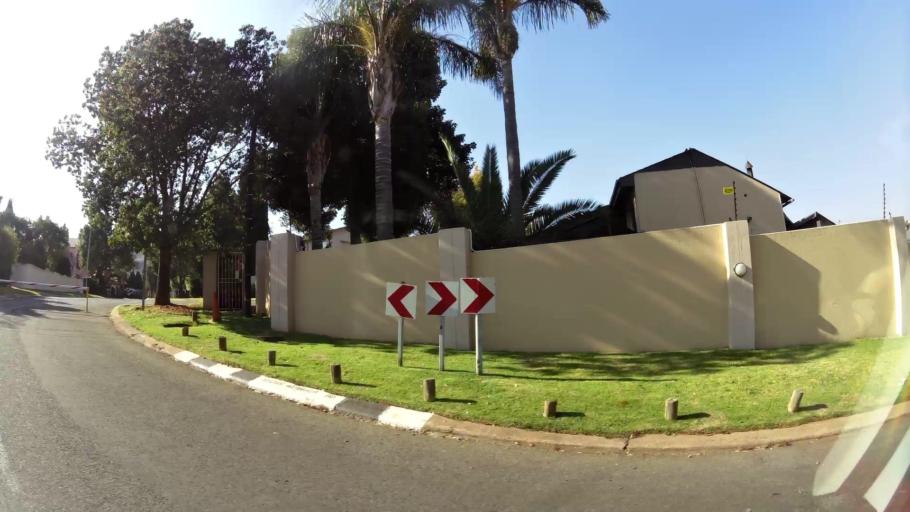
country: ZA
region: Gauteng
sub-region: City of Johannesburg Metropolitan Municipality
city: Johannesburg
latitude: -26.1747
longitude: 28.1081
